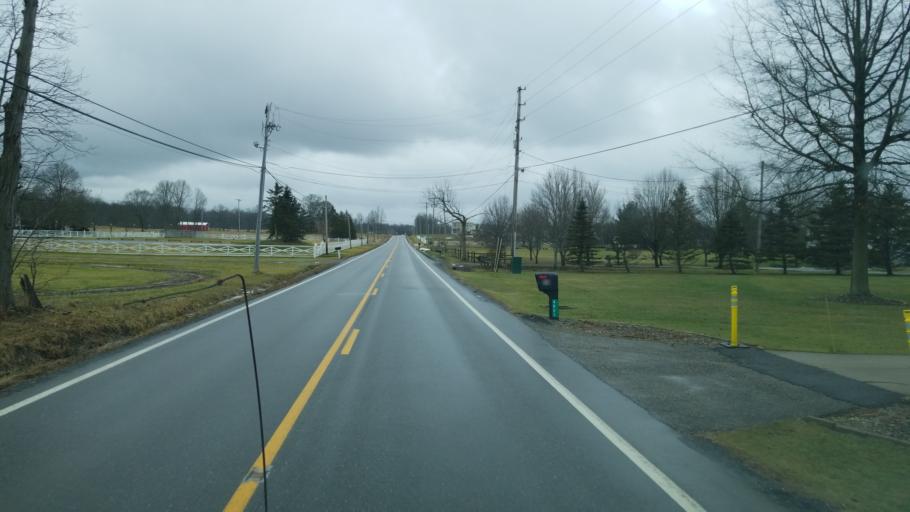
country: US
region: Ohio
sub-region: Trumbull County
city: Champion Heights
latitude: 41.3499
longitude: -80.9545
